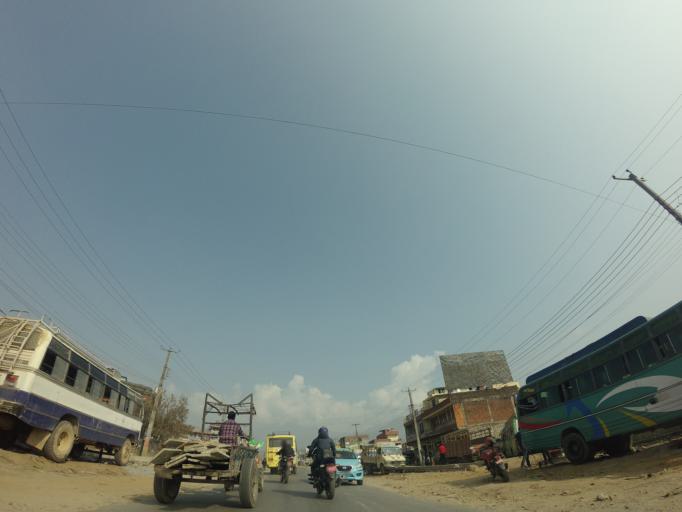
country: NP
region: Western Region
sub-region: Gandaki Zone
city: Pokhara
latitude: 28.2307
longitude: 83.9821
